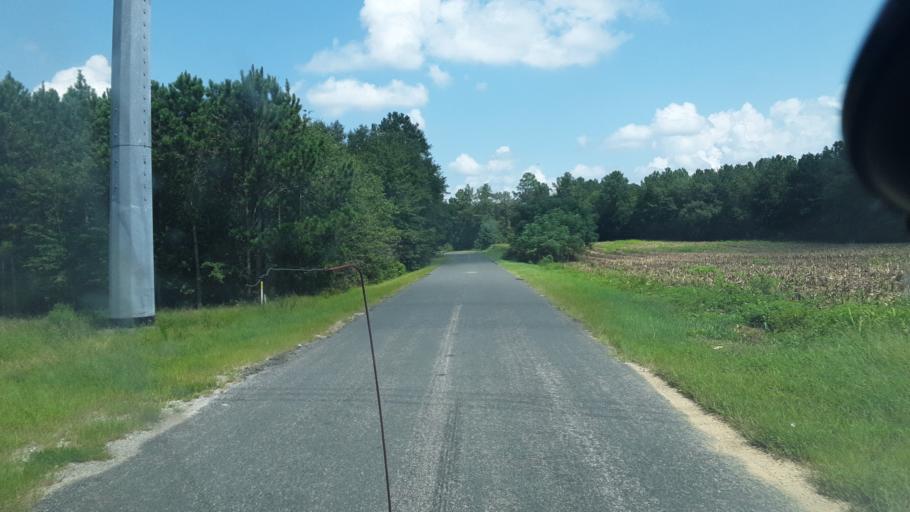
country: US
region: South Carolina
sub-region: Calhoun County
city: Oak Grove
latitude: 33.6823
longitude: -80.9696
